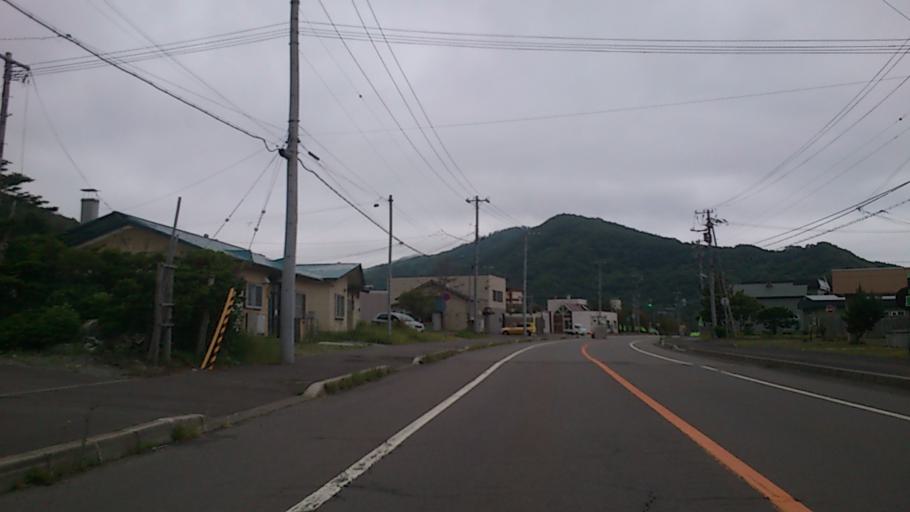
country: JP
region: Hokkaido
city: Iwanai
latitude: 42.7028
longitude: 140.0629
